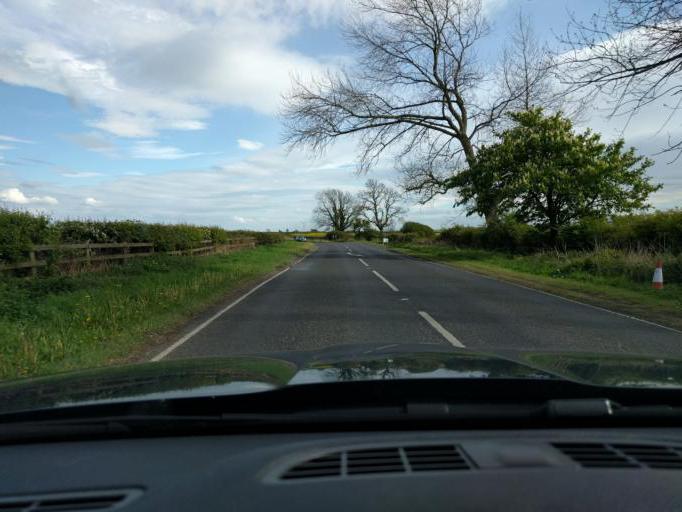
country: GB
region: England
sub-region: Northumberland
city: Stannington
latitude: 55.1345
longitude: -1.6480
